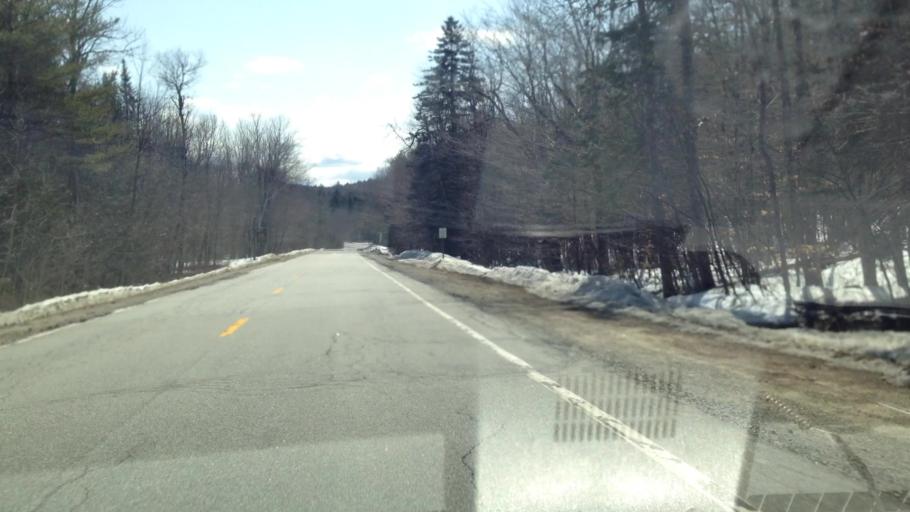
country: US
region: New Hampshire
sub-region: Sullivan County
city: Springfield
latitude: 43.4841
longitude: -71.9765
